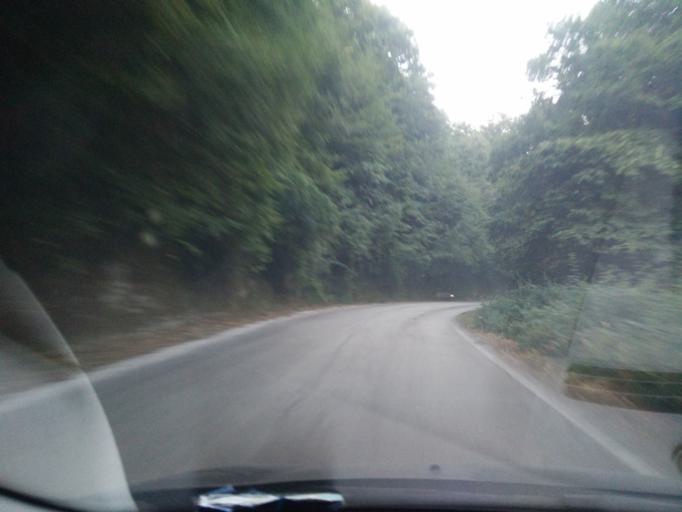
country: IT
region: Apulia
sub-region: Provincia di Foggia
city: Vico del Gargano
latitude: 41.8458
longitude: 16.0492
